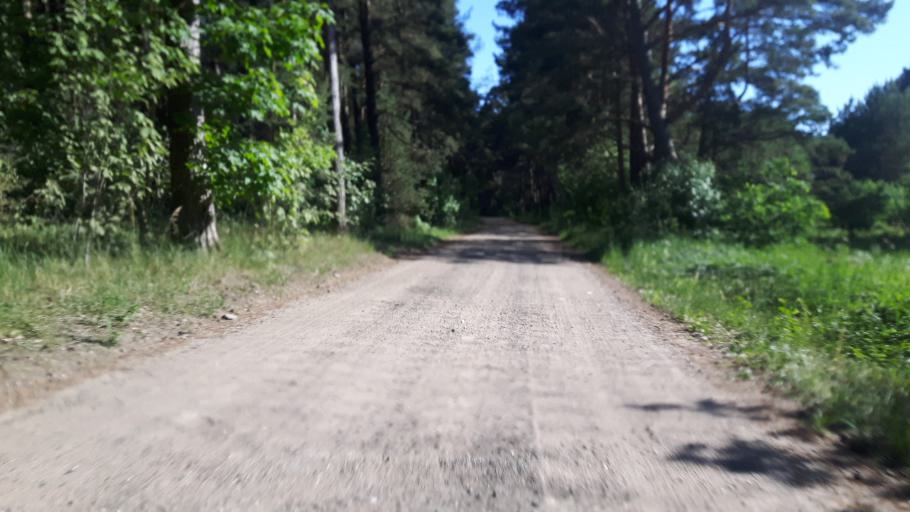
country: LV
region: Salacgrivas
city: Salacgriva
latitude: 57.7420
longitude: 24.3521
